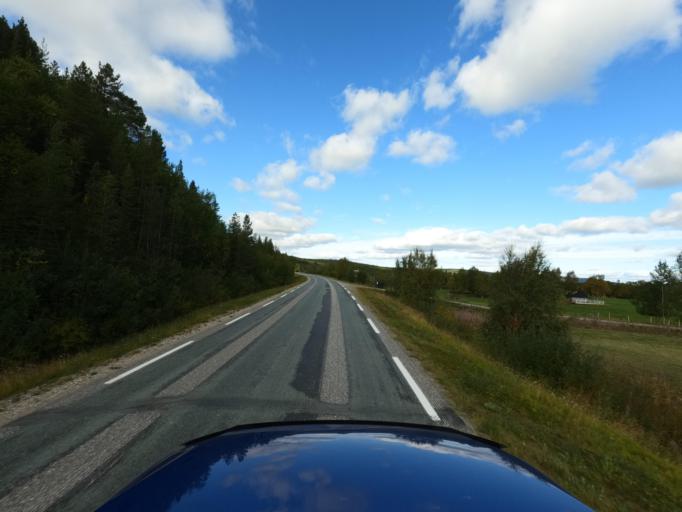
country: NO
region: Finnmark Fylke
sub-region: Karasjok
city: Karasjohka
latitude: 69.4123
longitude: 25.8032
